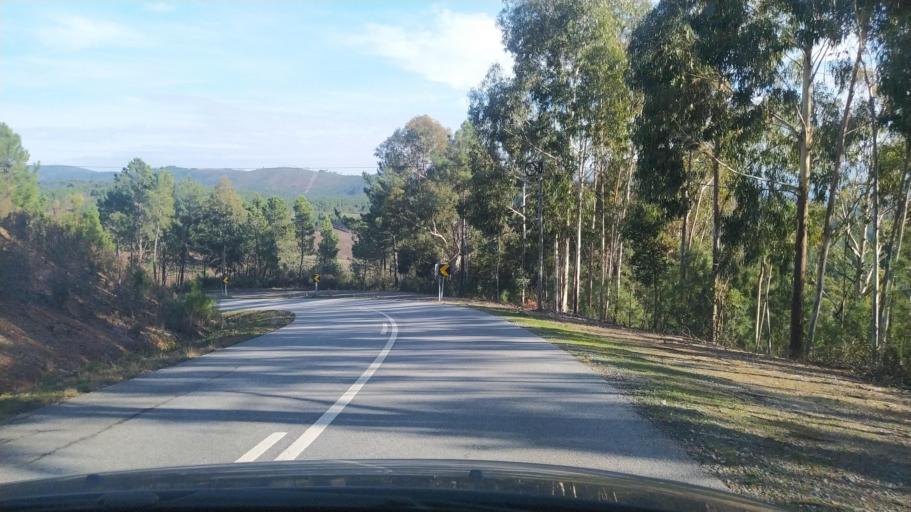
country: PT
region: Castelo Branco
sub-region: Concelho do Fundao
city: Aldeia de Joanes
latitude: 40.1740
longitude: -7.6773
